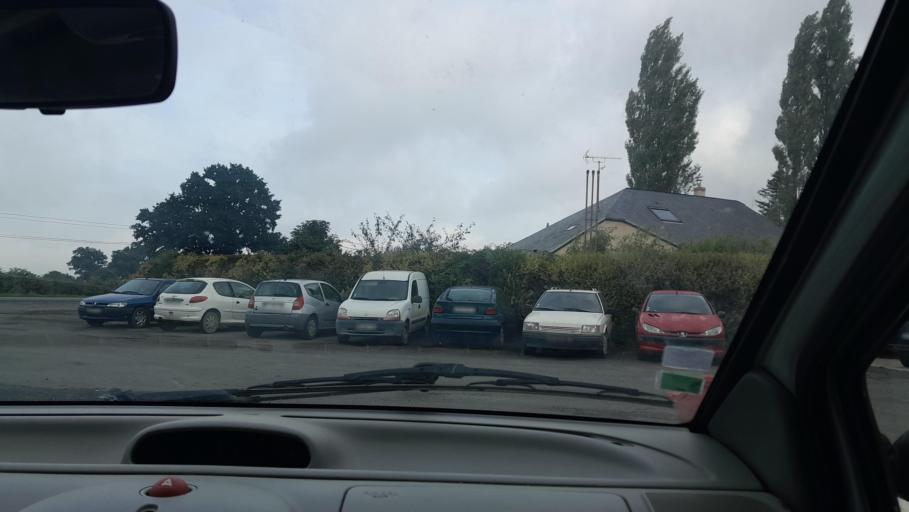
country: FR
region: Brittany
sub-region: Departement d'Ille-et-Vilaine
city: Le Pertre
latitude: 47.9667
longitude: -1.0413
